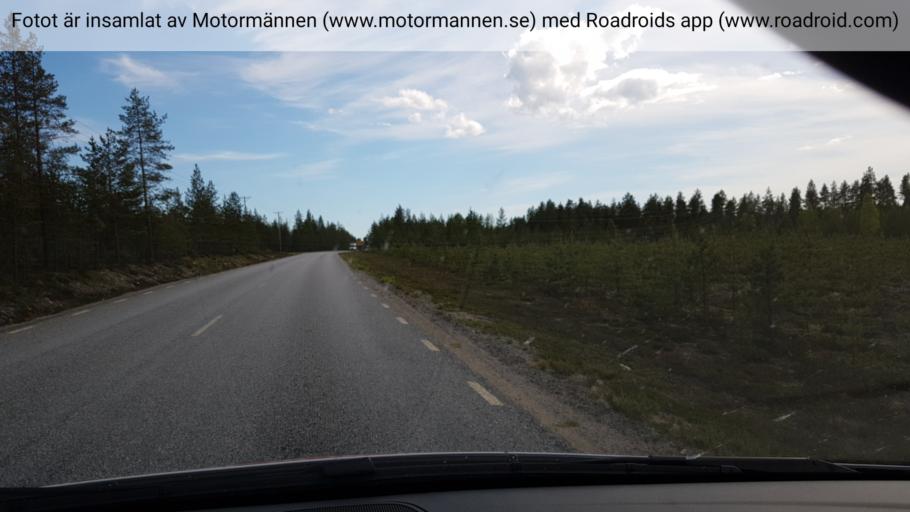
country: SE
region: Vaesterbotten
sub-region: Umea Kommun
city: Saevar
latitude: 63.9651
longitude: 20.5081
